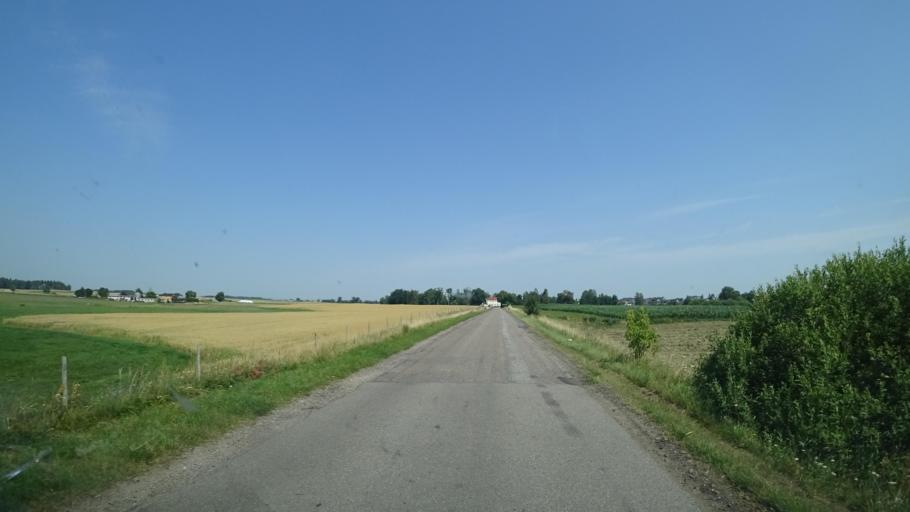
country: PL
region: Pomeranian Voivodeship
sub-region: Powiat chojnicki
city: Brusy
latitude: 53.8770
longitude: 17.6292
